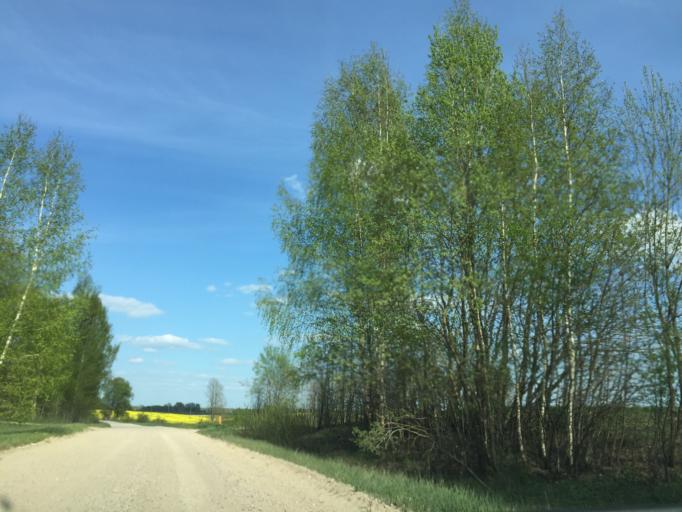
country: LV
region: Vecumnieki
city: Vecumnieki
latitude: 56.5136
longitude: 24.4384
